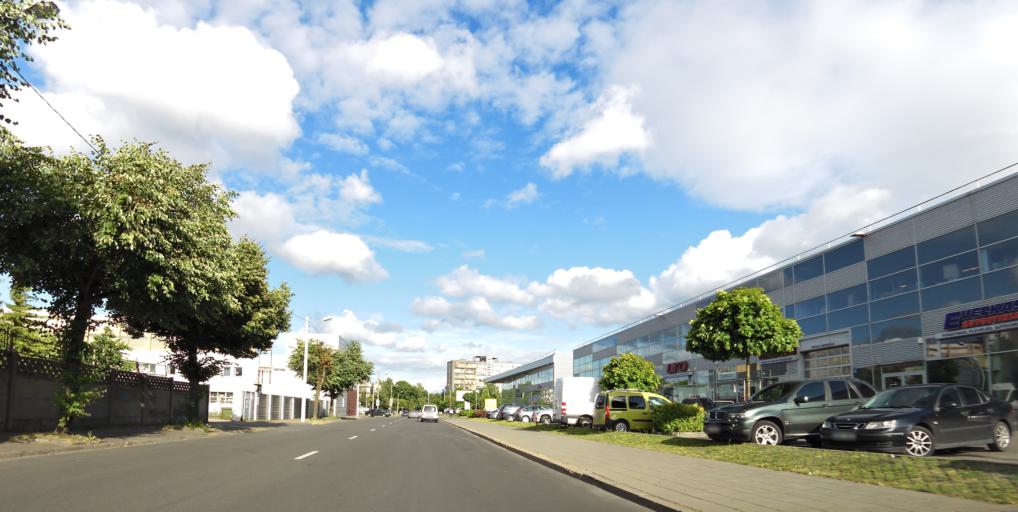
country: LT
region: Vilnius County
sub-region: Vilnius
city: Vilnius
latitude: 54.7145
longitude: 25.3019
